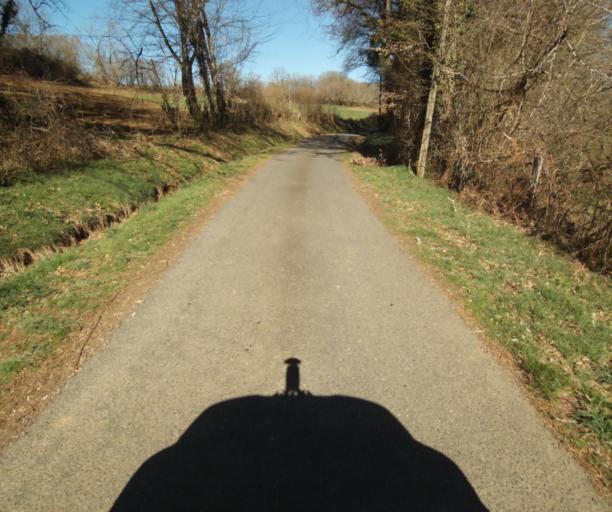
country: FR
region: Limousin
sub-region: Departement de la Correze
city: Chamboulive
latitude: 45.4138
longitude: 1.7224
